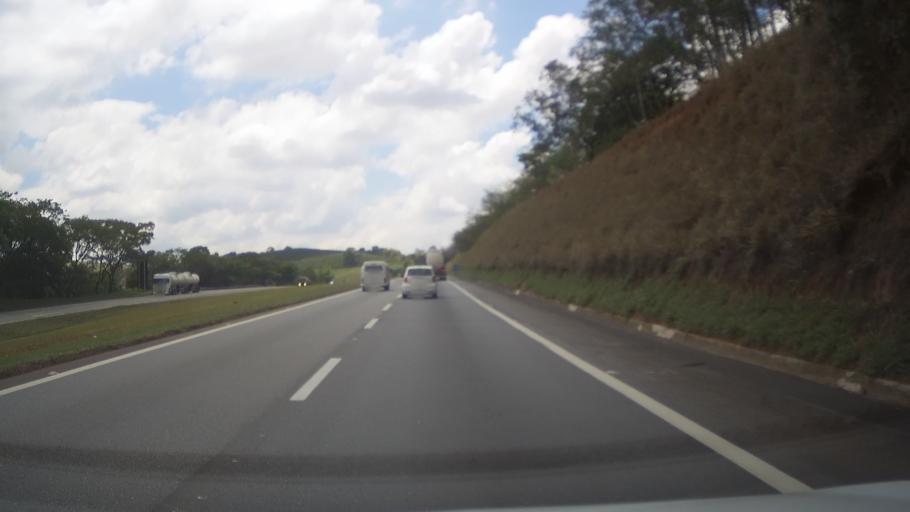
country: BR
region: Minas Gerais
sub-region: Tres Coracoes
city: Tres Coracoes
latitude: -21.7063
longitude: -45.3722
